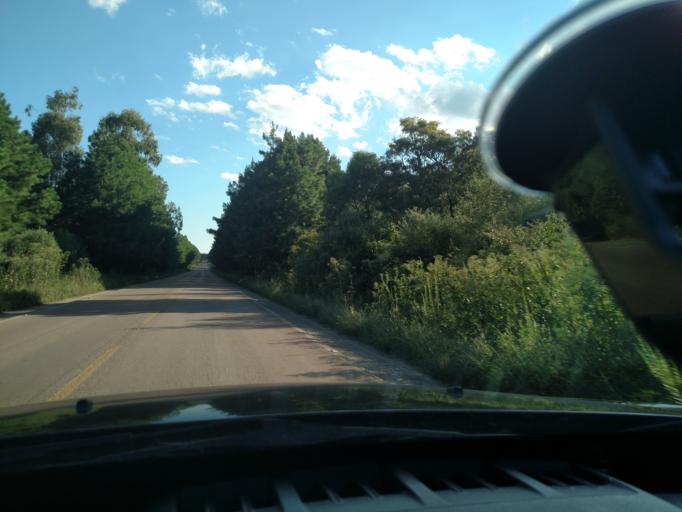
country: BR
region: Santa Catarina
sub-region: Otacilio Costa
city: Otacilio Costa
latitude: -27.4351
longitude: -50.1232
